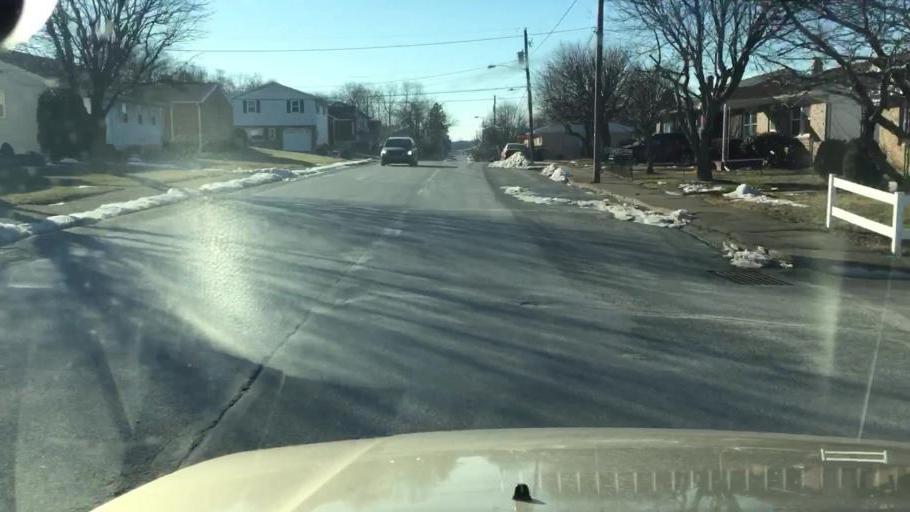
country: US
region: Pennsylvania
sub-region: Luzerne County
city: West Hazleton
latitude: 40.9680
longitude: -75.9914
